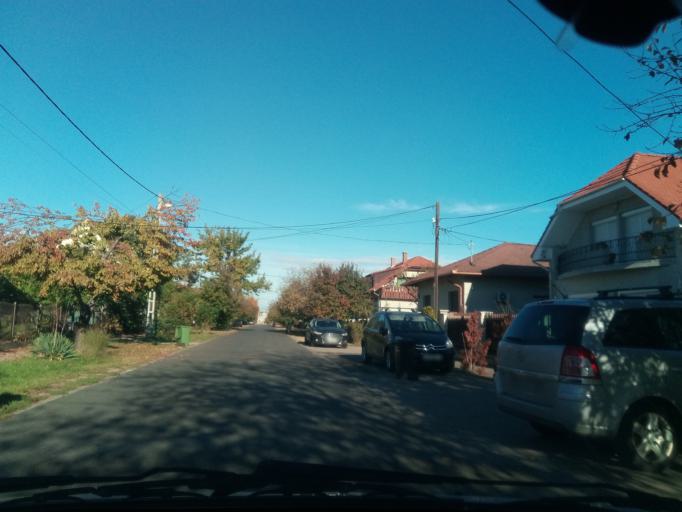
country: HU
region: Pest
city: Gyal
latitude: 47.4305
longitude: 19.2265
